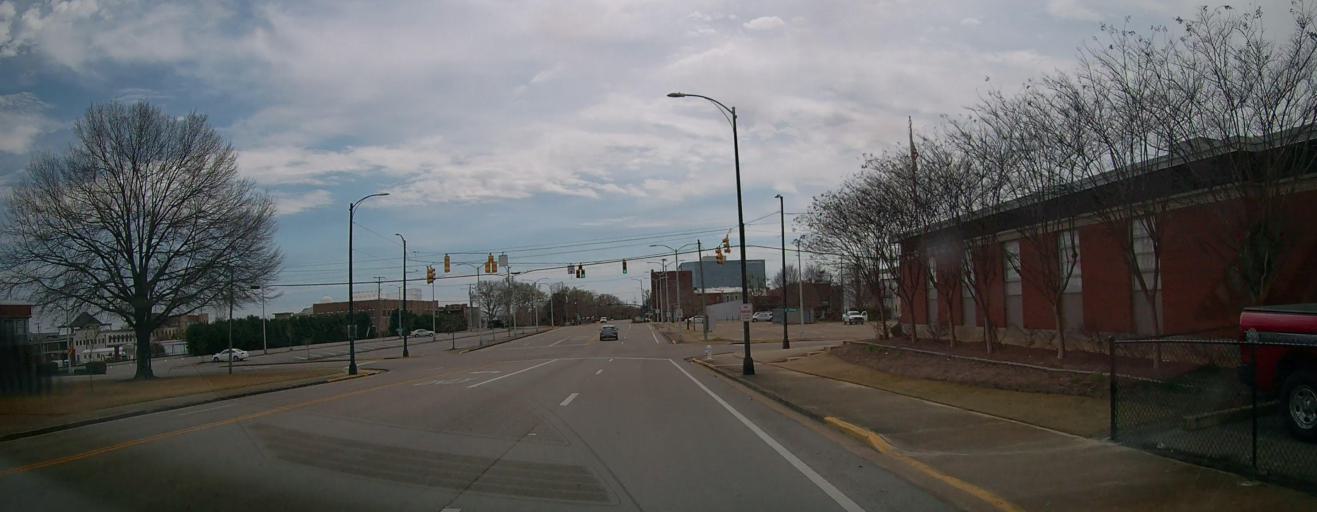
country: US
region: Mississippi
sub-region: Lee County
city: Tupelo
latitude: 34.2598
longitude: -88.7035
